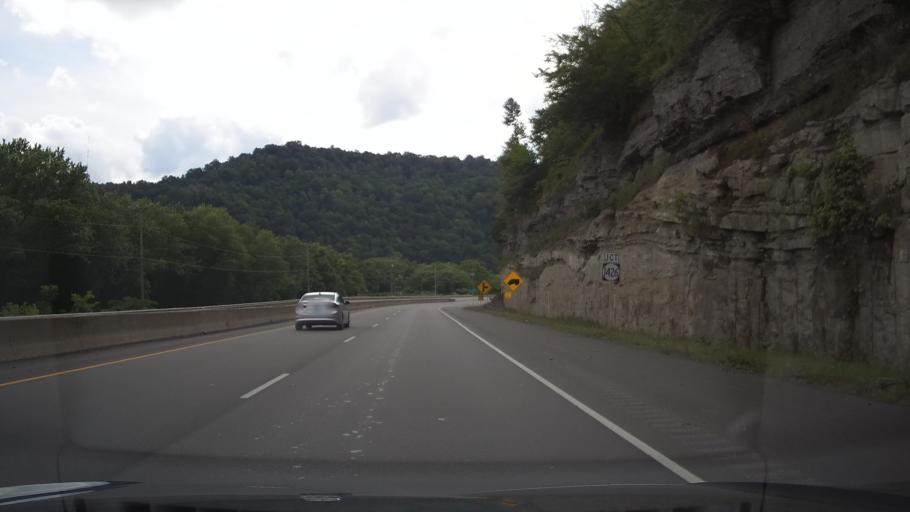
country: US
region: Kentucky
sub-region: Floyd County
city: Prestonsburg
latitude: 37.6036
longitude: -82.6952
